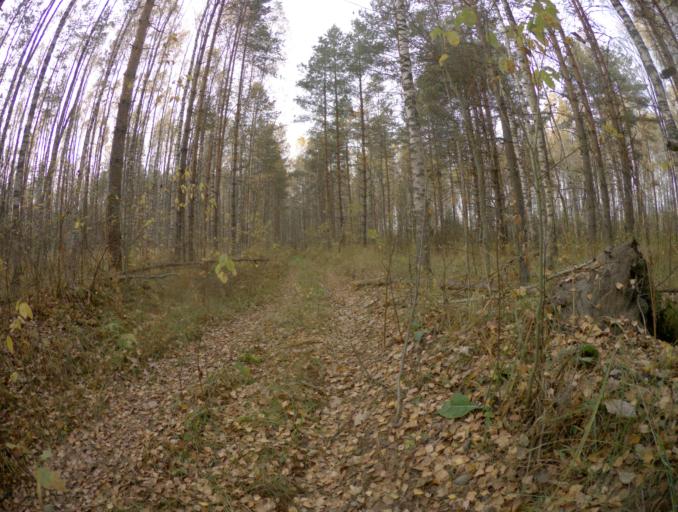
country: RU
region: Vladimir
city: Sobinka
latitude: 55.9672
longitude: 40.0912
